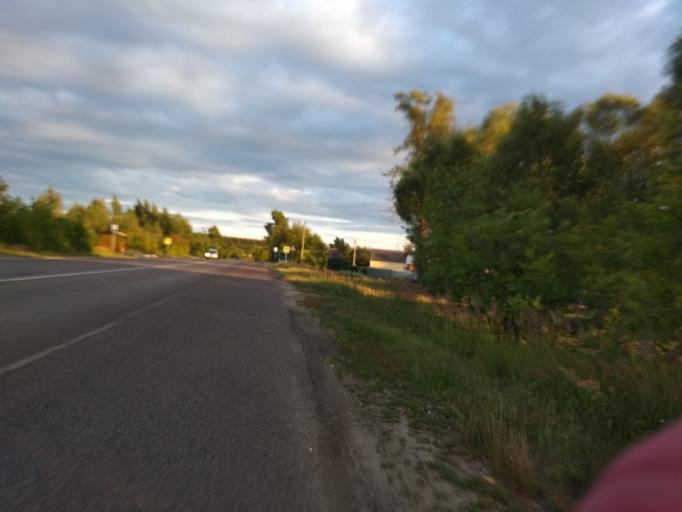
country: RU
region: Moskovskaya
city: Kerva
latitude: 55.5911
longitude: 39.7007
